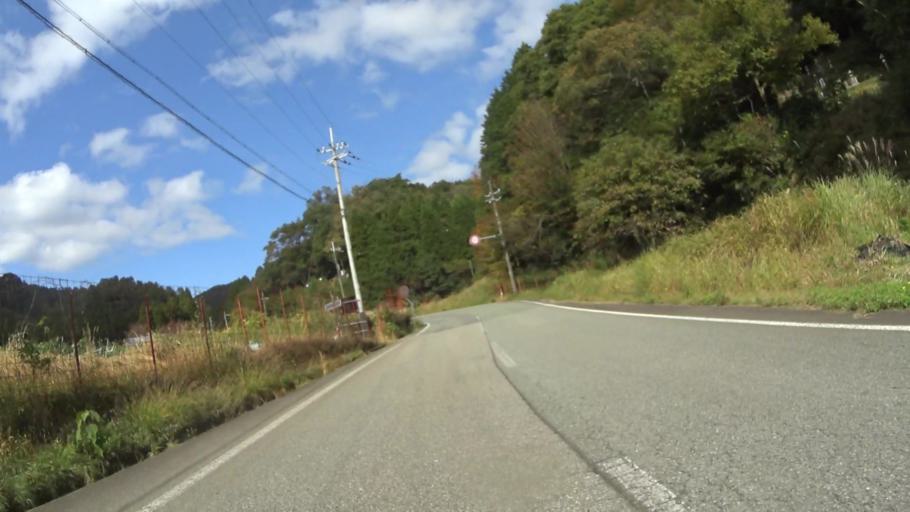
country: JP
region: Hyogo
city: Toyooka
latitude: 35.5123
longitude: 134.9916
